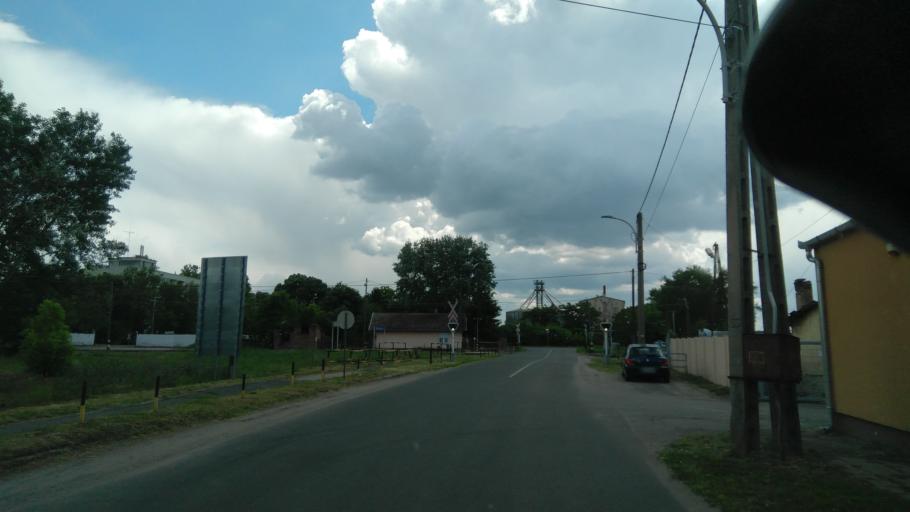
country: HU
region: Bekes
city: Gyula
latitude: 46.6572
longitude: 21.2696
